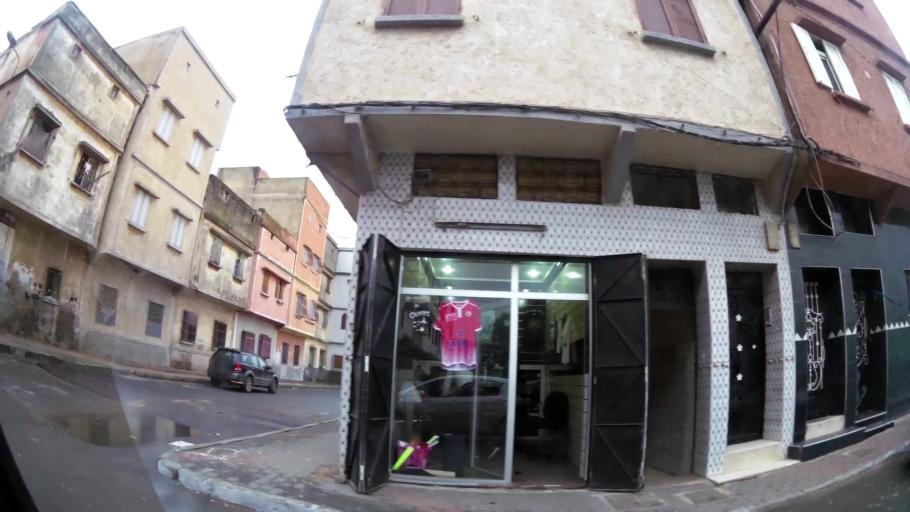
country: MA
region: Grand Casablanca
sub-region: Casablanca
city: Casablanca
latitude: 33.5533
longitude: -7.5815
